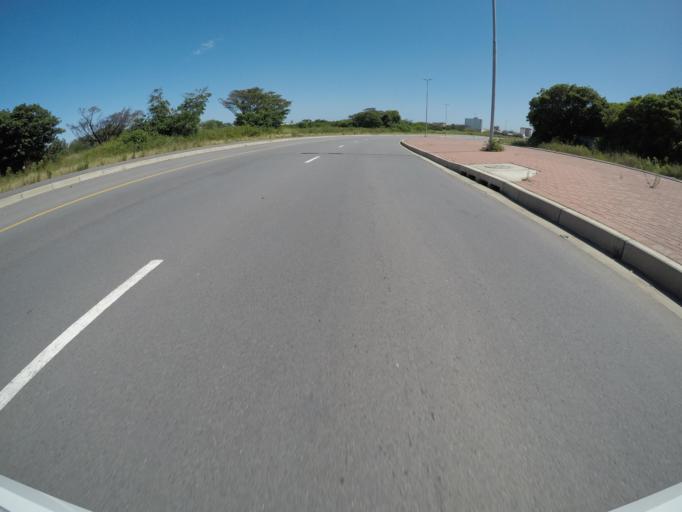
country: ZA
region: Eastern Cape
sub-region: Buffalo City Metropolitan Municipality
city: East London
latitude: -33.0107
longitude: 27.9143
